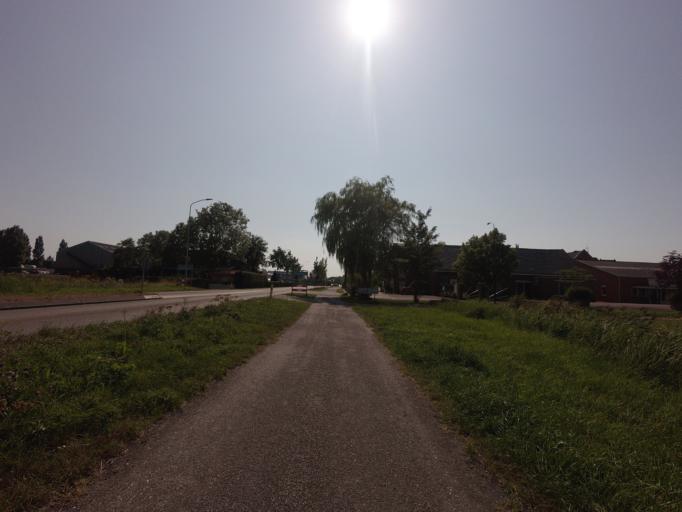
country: NL
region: Groningen
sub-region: Gemeente Zuidhorn
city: Grijpskerk
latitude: 53.2684
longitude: 6.3070
